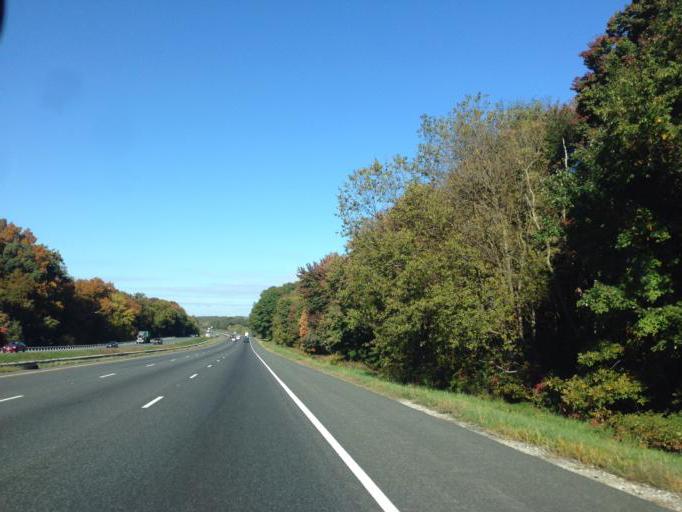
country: US
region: Maryland
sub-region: Carroll County
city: Sykesville
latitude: 39.3327
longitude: -77.0317
